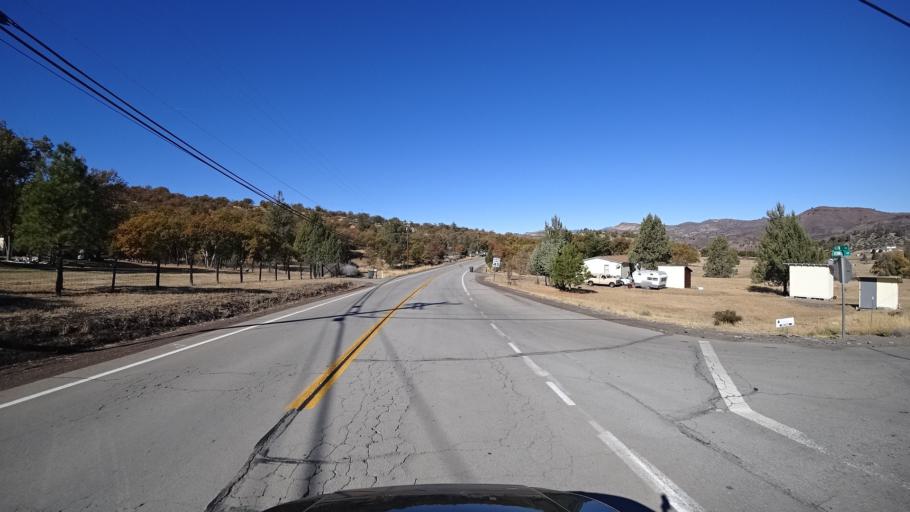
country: US
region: California
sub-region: Siskiyou County
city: Montague
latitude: 41.8869
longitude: -122.4900
